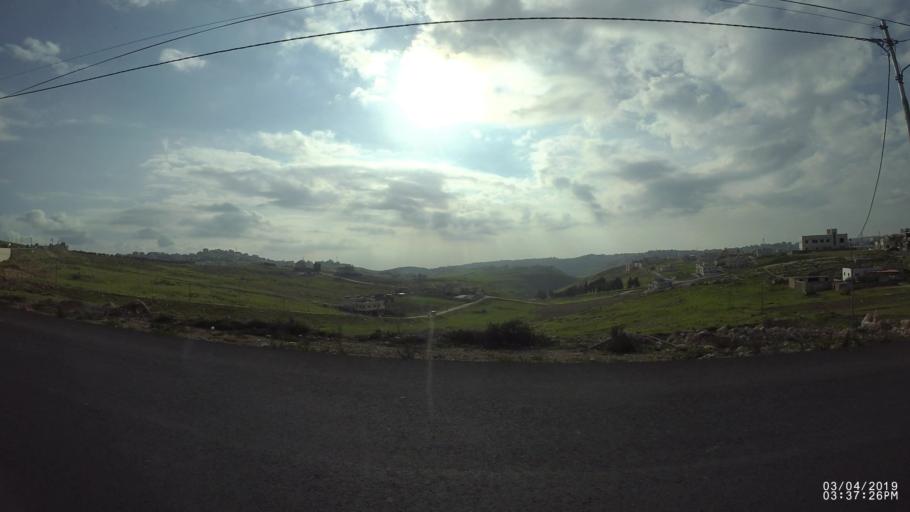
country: JO
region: Amman
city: Wadi as Sir
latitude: 31.9284
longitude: 35.8489
